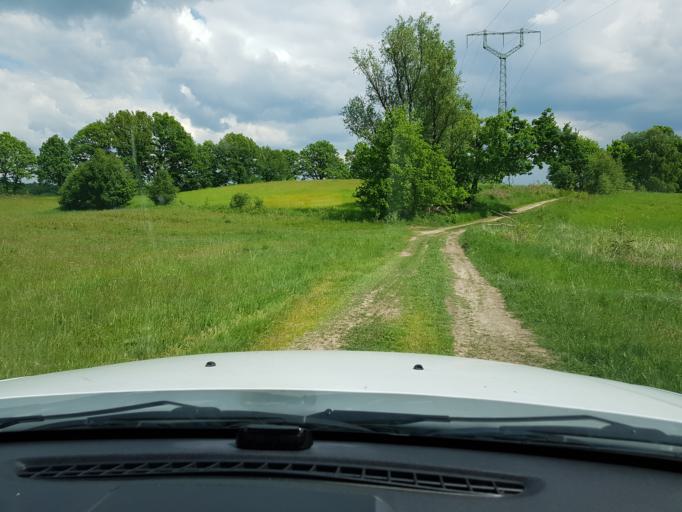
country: PL
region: West Pomeranian Voivodeship
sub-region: Powiat drawski
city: Drawsko Pomorskie
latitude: 53.5515
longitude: 15.7145
